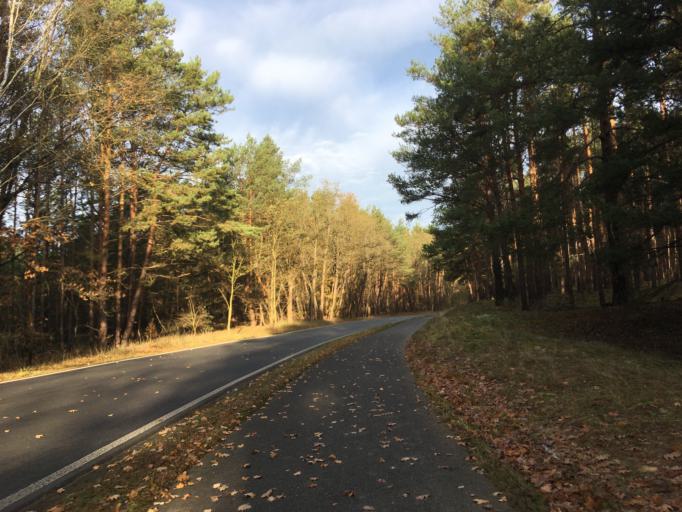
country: DE
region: Brandenburg
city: Luebben
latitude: 51.9545
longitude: 13.8822
